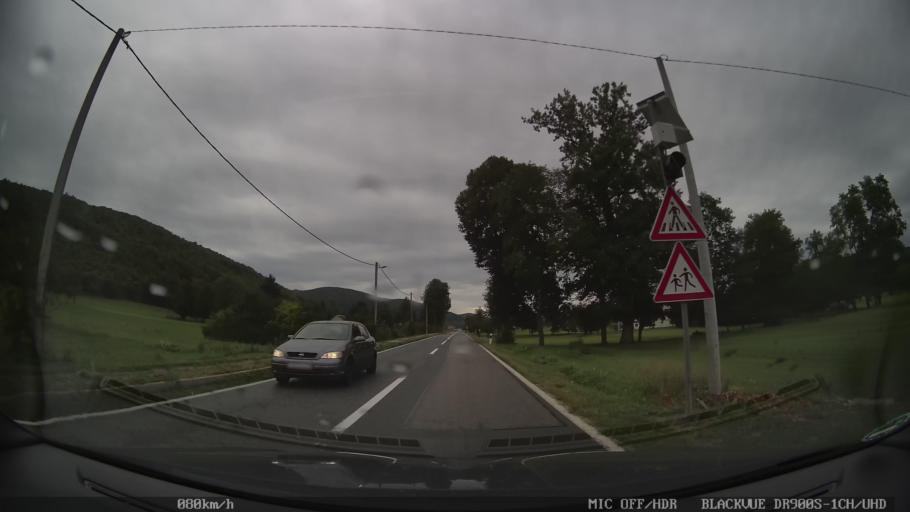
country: HR
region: Licko-Senjska
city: Brinje
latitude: 44.9162
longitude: 15.1558
